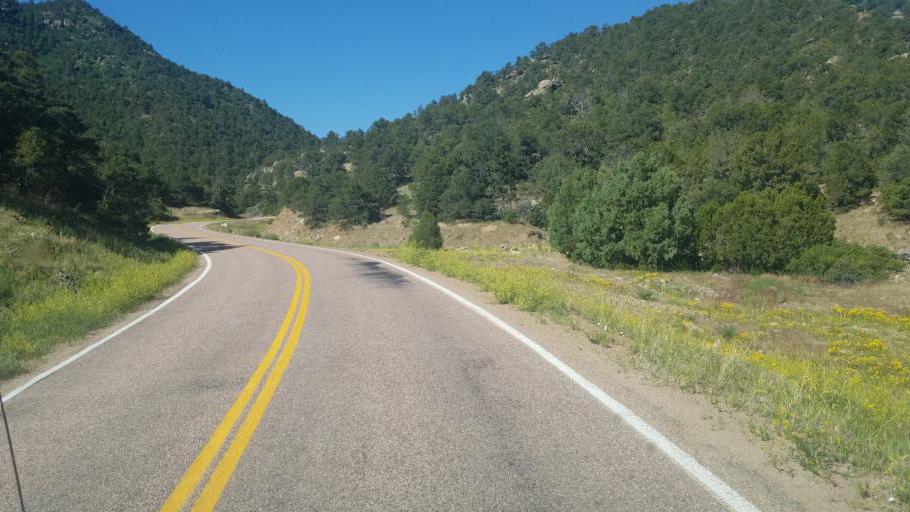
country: US
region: Colorado
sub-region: Fremont County
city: Canon City
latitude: 38.4247
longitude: -105.4053
